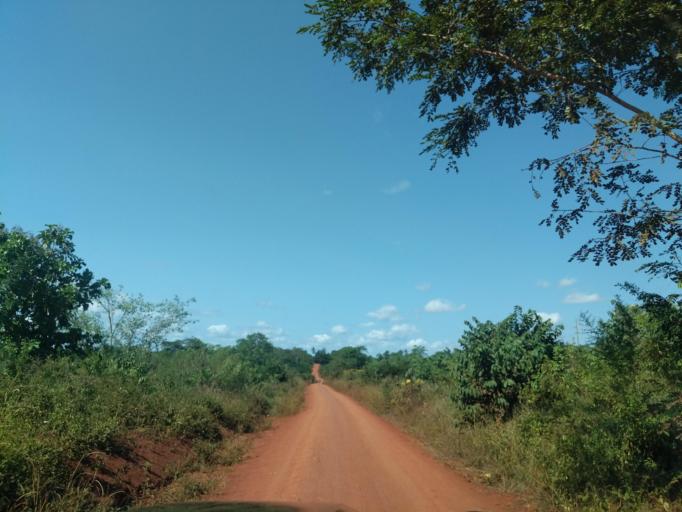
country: TZ
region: Tanga
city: Muheza
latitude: -5.3771
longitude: 38.5810
